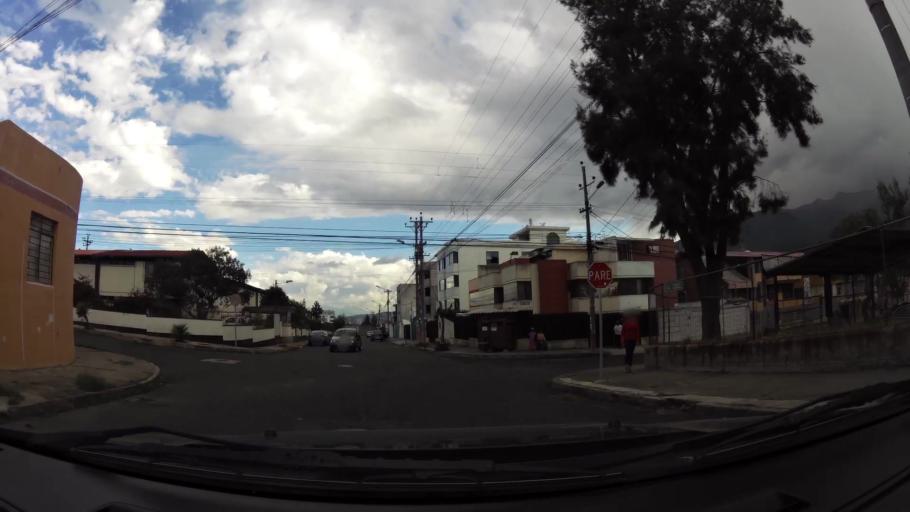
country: EC
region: Pichincha
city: Quito
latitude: -0.1326
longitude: -78.4843
